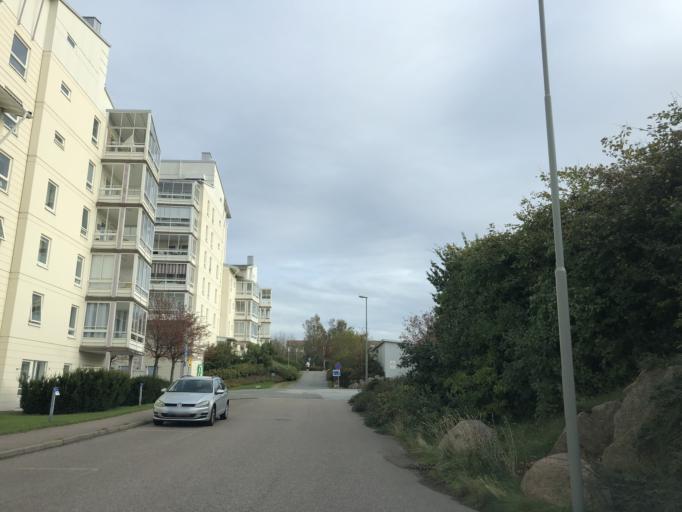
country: SE
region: Vaestra Goetaland
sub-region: Goteborg
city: Majorna
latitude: 57.6767
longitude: 11.8809
